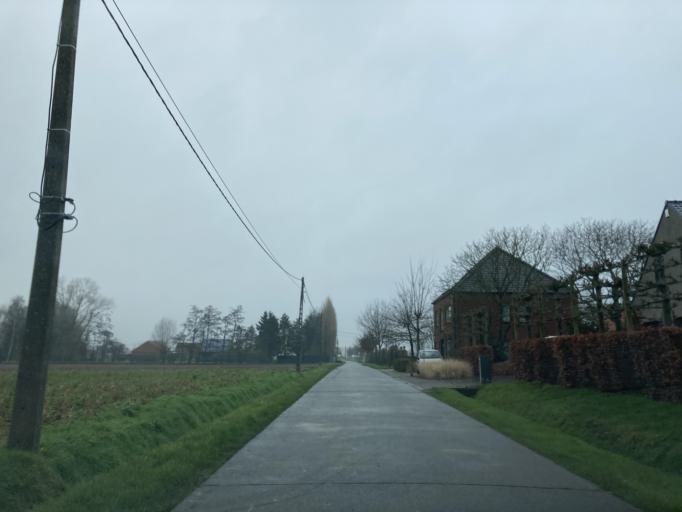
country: BE
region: Flanders
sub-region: Provincie West-Vlaanderen
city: Ichtegem
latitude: 51.1249
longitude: 3.0523
